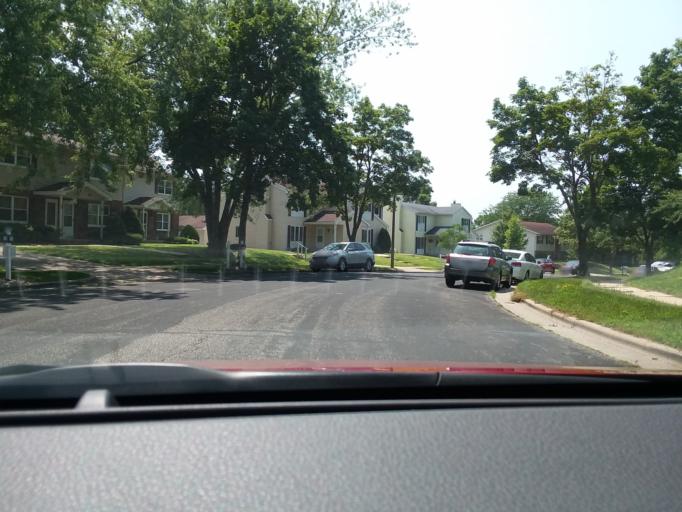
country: US
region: Wisconsin
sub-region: Dane County
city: Madison
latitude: 43.0279
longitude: -89.4164
